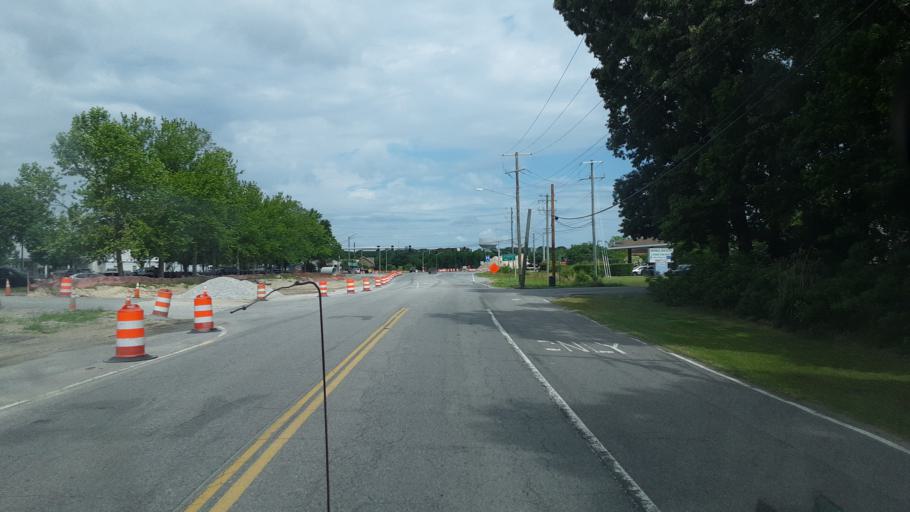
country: US
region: Virginia
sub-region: City of Virginia Beach
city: Virginia Beach
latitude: 36.7507
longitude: -76.0082
